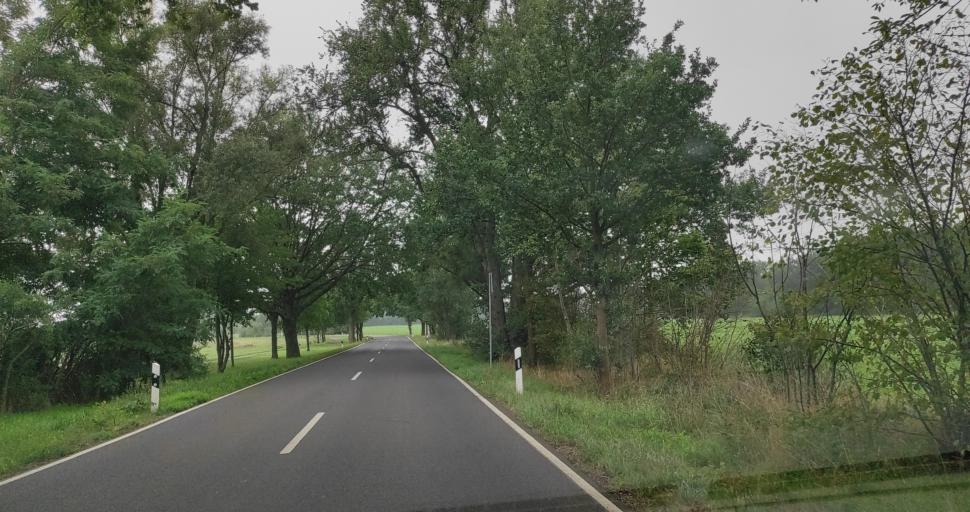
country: DE
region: Brandenburg
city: Forst
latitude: 51.7058
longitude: 14.6259
